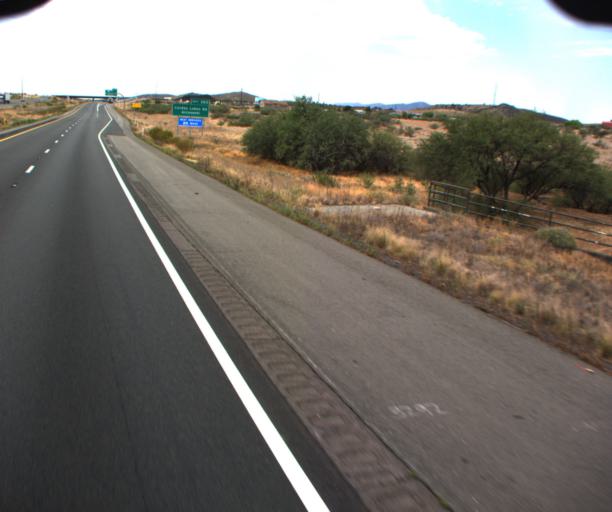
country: US
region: Arizona
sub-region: Yavapai County
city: Cordes Lakes
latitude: 34.3425
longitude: -112.1181
